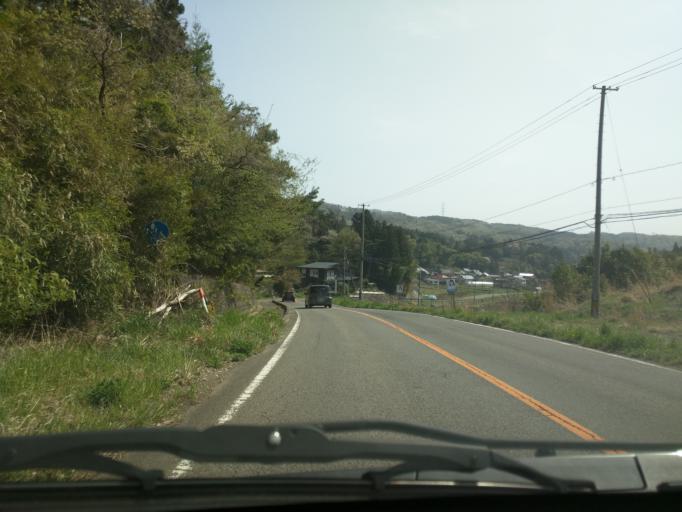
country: JP
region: Fukushima
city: Nihommatsu
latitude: 37.6007
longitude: 140.3884
